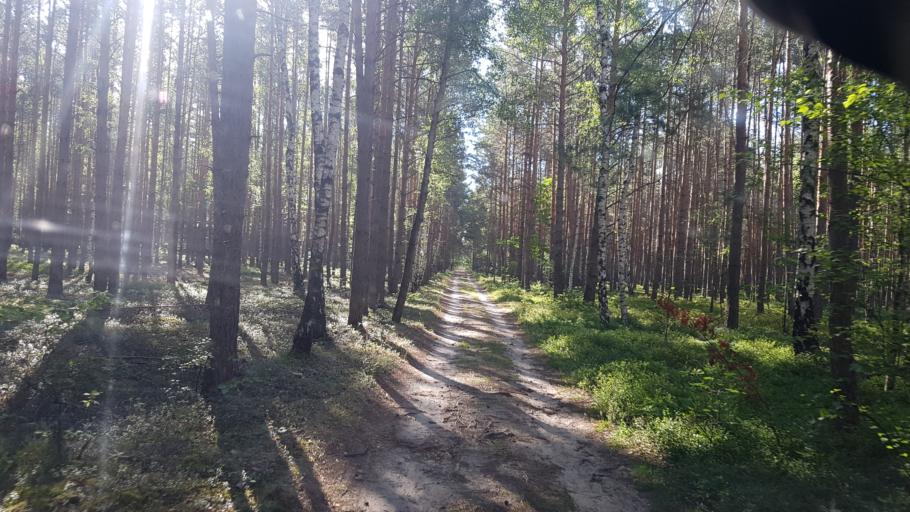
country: DE
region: Brandenburg
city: Finsterwalde
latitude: 51.6096
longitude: 13.7743
